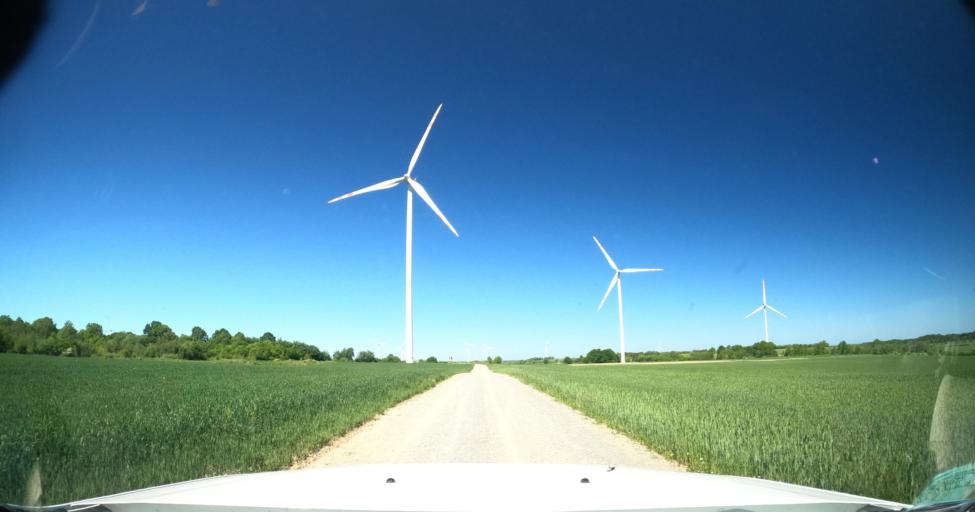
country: PL
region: Pomeranian Voivodeship
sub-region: Powiat slupski
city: Ustka
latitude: 54.5100
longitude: 16.7489
